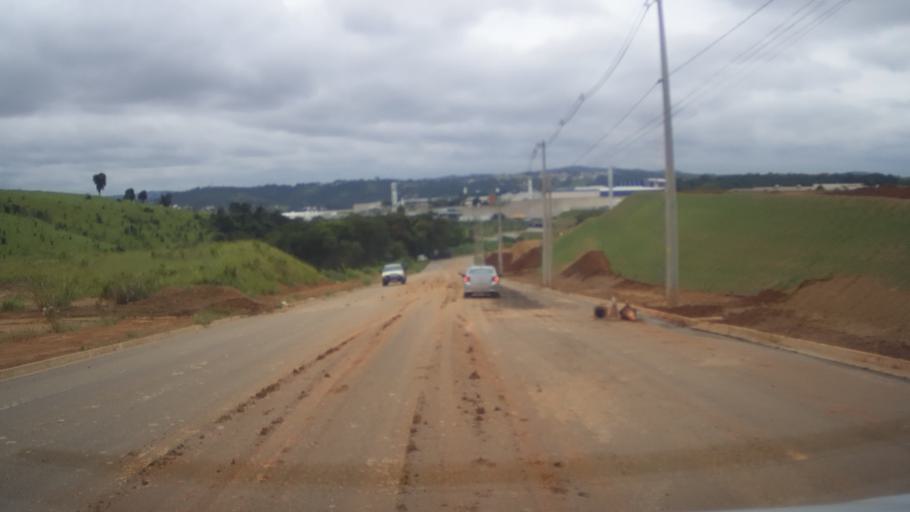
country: BR
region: Sao Paulo
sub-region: Vinhedo
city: Vinhedo
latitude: -23.0752
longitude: -47.0062
